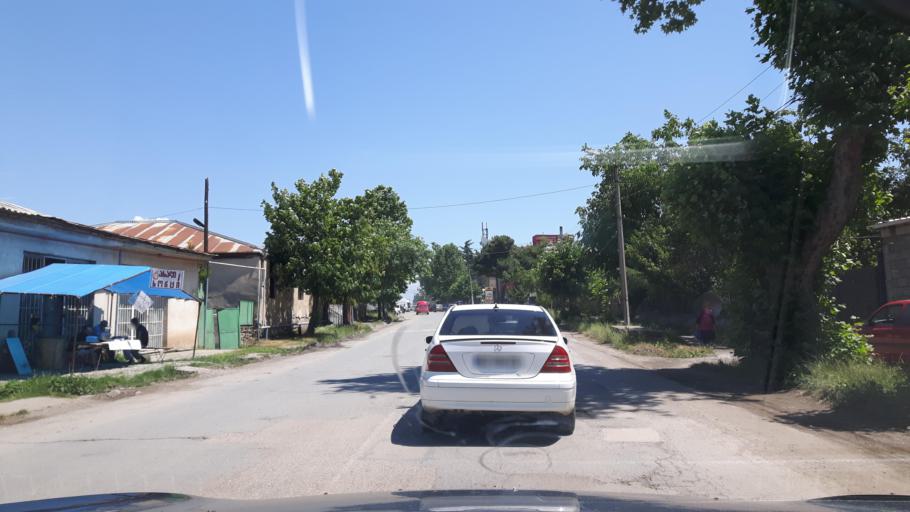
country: GE
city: Tsnori
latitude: 41.6219
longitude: 45.9768
